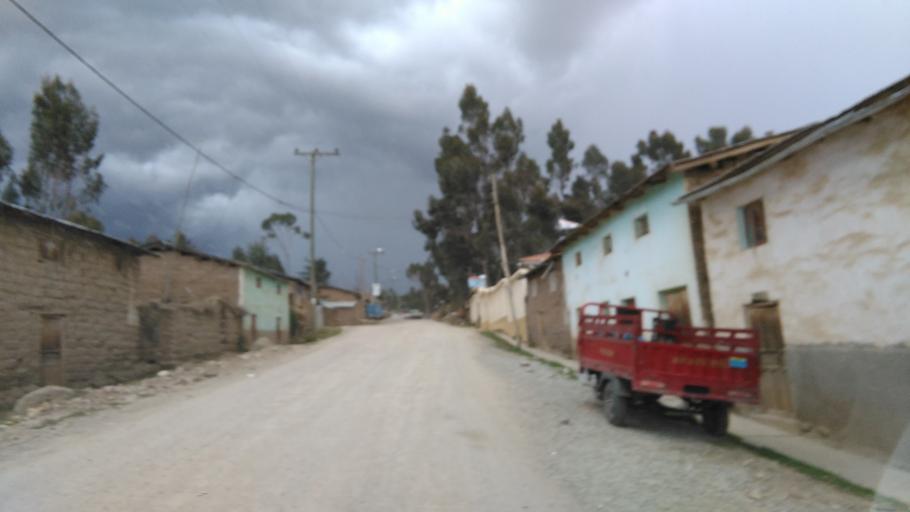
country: PE
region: Apurimac
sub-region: Provincia de Andahuaylas
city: San Jeronimo
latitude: -13.7348
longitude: -73.3487
